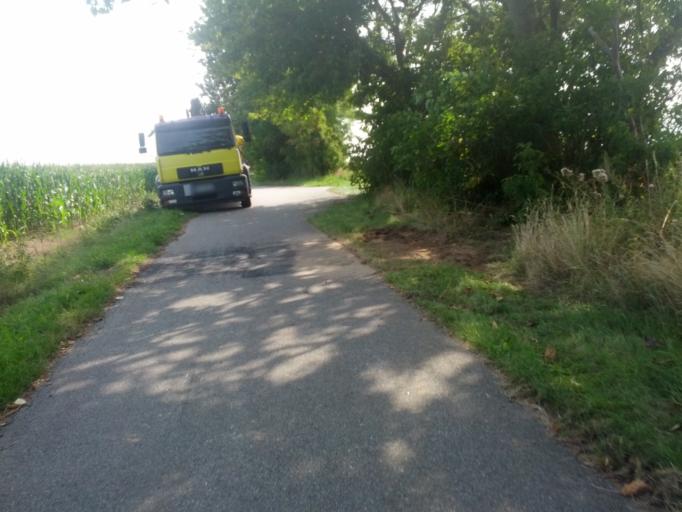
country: DE
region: Mecklenburg-Vorpommern
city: Bastorf
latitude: 54.1268
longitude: 11.6814
